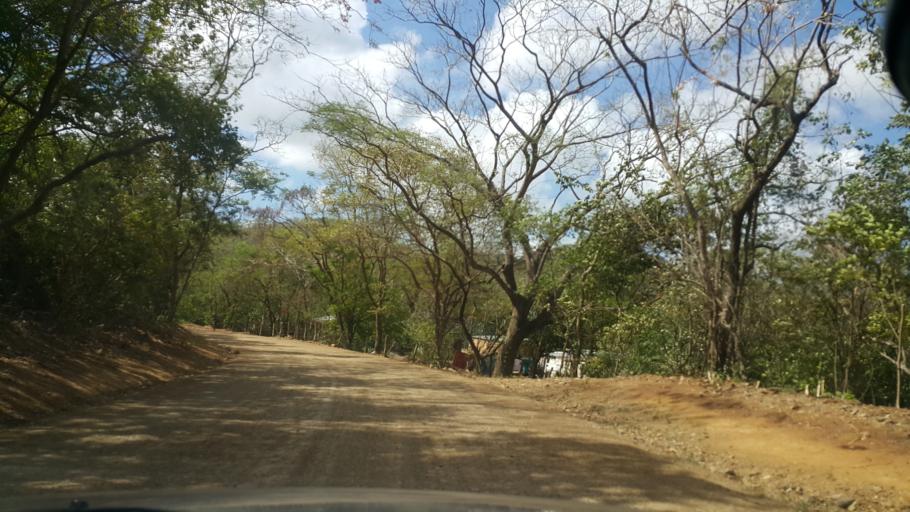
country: NI
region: Rivas
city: San Juan del Sur
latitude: 11.2997
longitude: -85.8655
